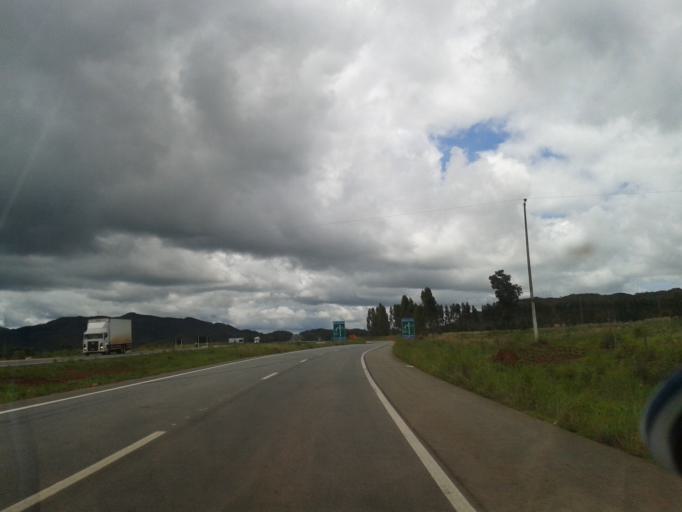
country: BR
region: Goias
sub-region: Goias
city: Goias
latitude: -16.0035
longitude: -50.0314
